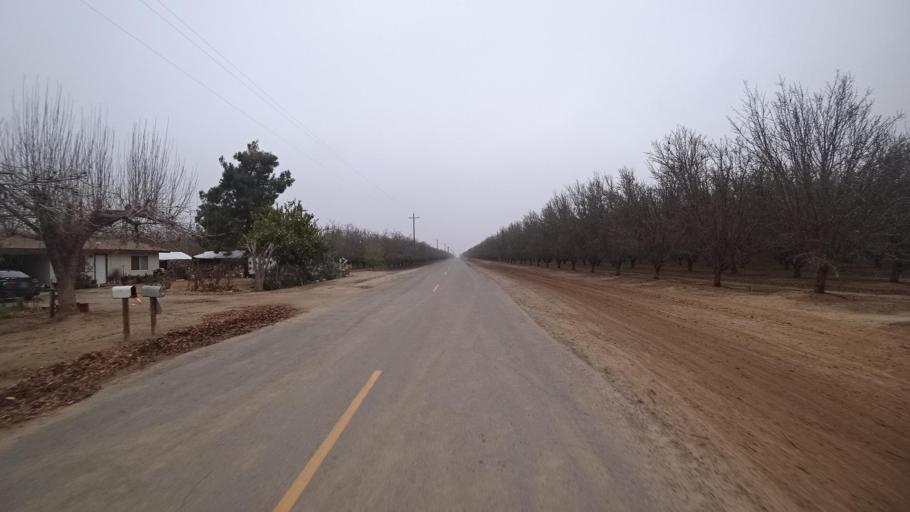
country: US
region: California
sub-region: Kern County
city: Wasco
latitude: 35.5794
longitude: -119.5095
